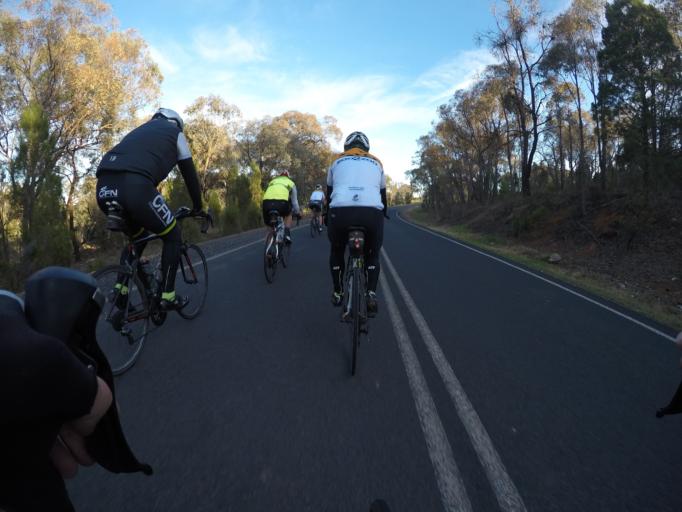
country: AU
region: New South Wales
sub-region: Cabonne
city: Molong
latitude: -33.0705
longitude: 148.8260
